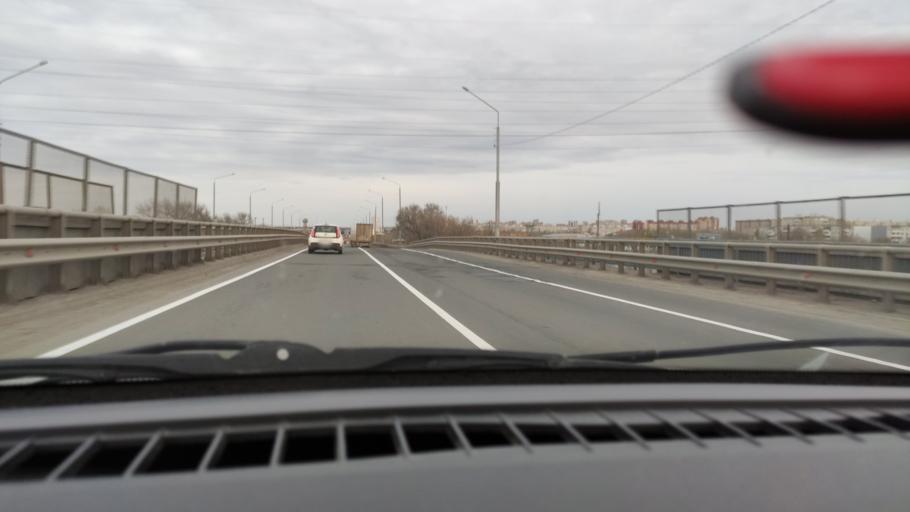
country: RU
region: Orenburg
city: Orenburg
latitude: 51.8521
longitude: 55.1402
